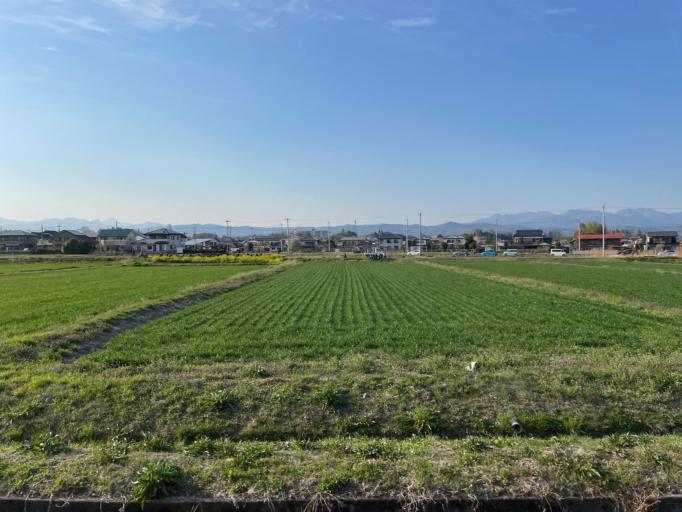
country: JP
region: Gunma
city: Annaka
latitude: 36.3005
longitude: 138.8621
